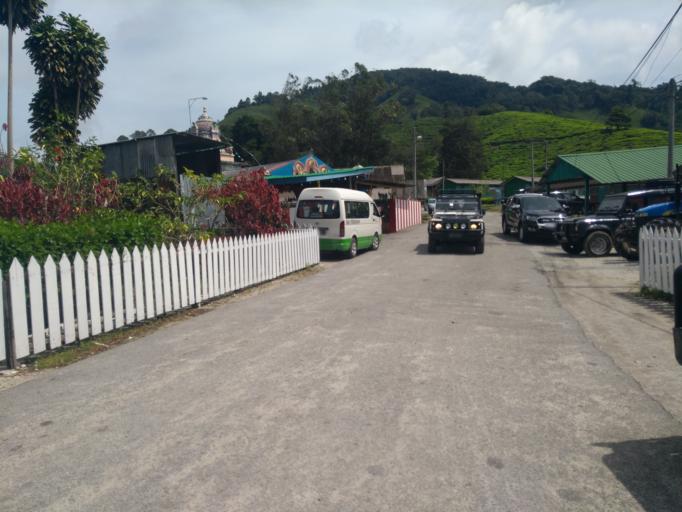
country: MY
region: Pahang
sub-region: Cameron Highlands
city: Tanah Rata
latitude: 4.5161
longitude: 101.4133
